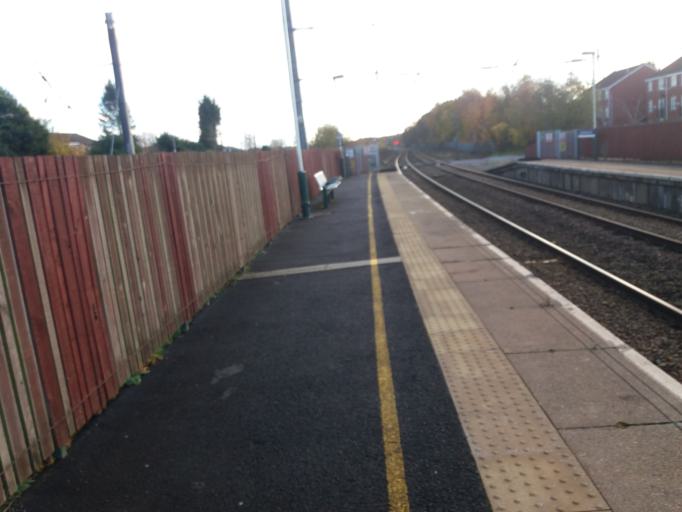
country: GB
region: England
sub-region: Lancashire
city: Euxton
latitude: 53.6598
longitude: -2.6716
